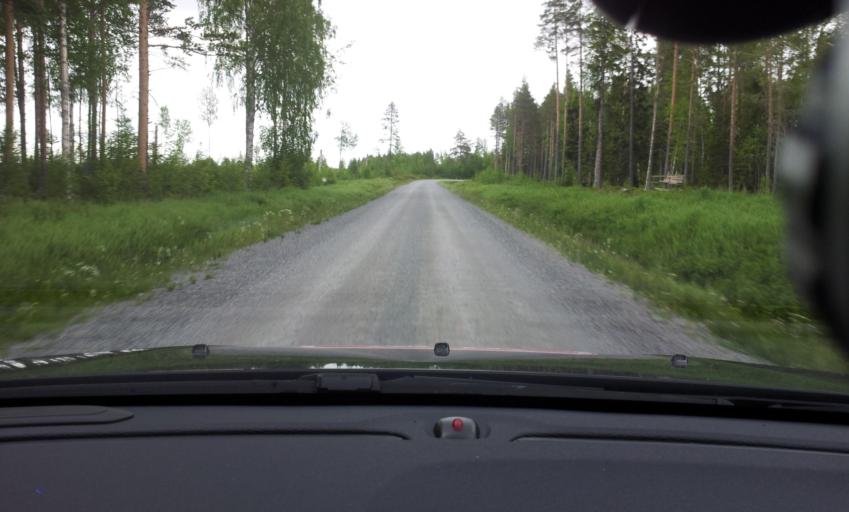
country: SE
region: Jaemtland
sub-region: OEstersunds Kommun
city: Brunflo
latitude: 63.1409
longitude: 15.0603
